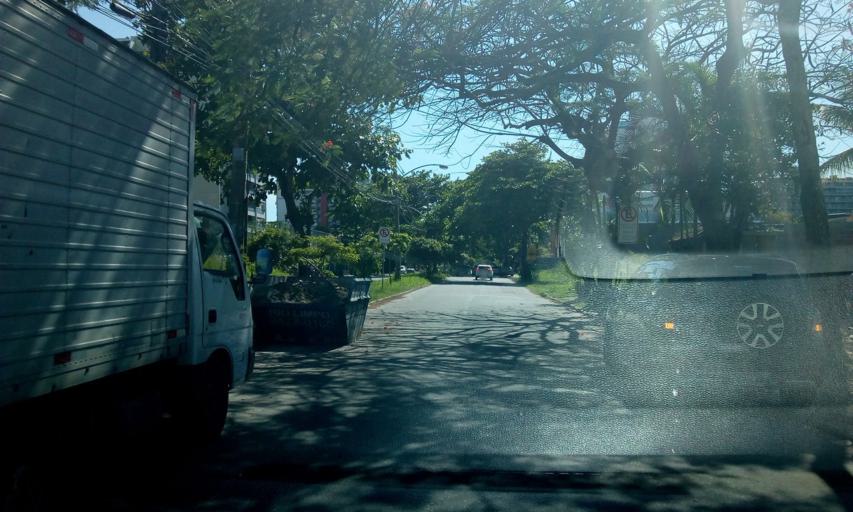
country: BR
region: Rio de Janeiro
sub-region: Nilopolis
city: Nilopolis
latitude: -23.0238
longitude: -43.4871
